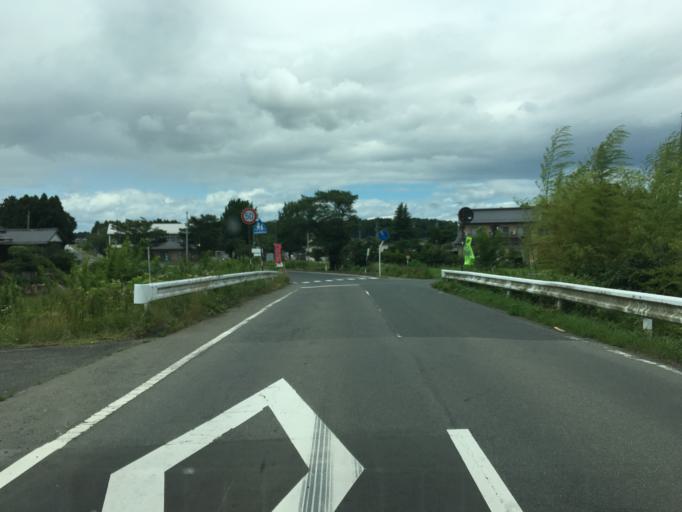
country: JP
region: Fukushima
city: Namie
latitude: 37.7240
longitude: 140.9306
